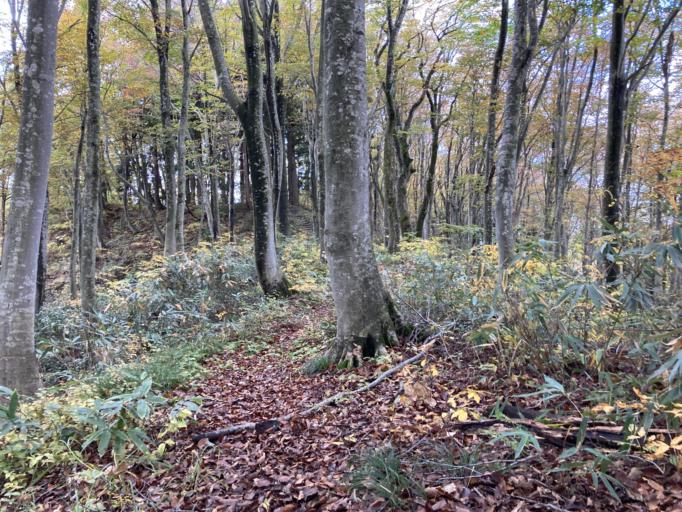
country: JP
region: Niigata
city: Tokamachi
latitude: 37.1546
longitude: 138.6282
